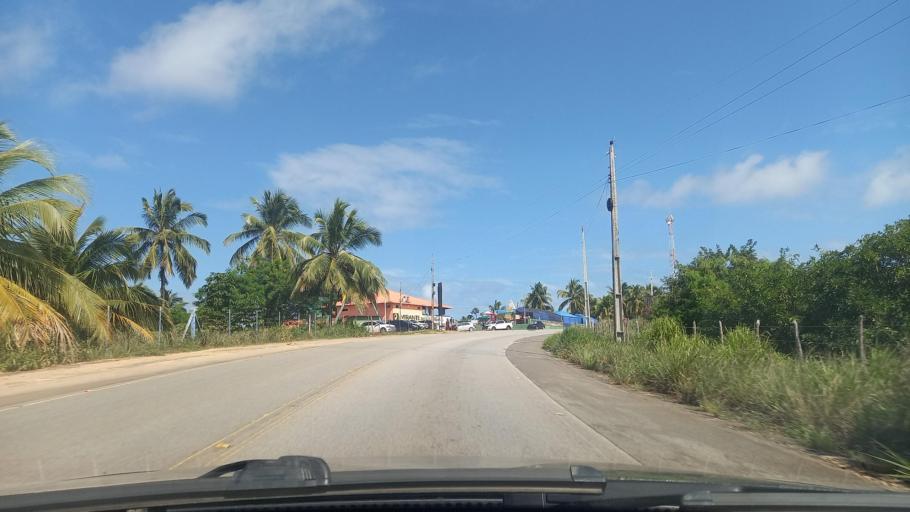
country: BR
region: Alagoas
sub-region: Marechal Deodoro
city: Marechal Deodoro
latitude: -9.8642
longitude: -35.9148
